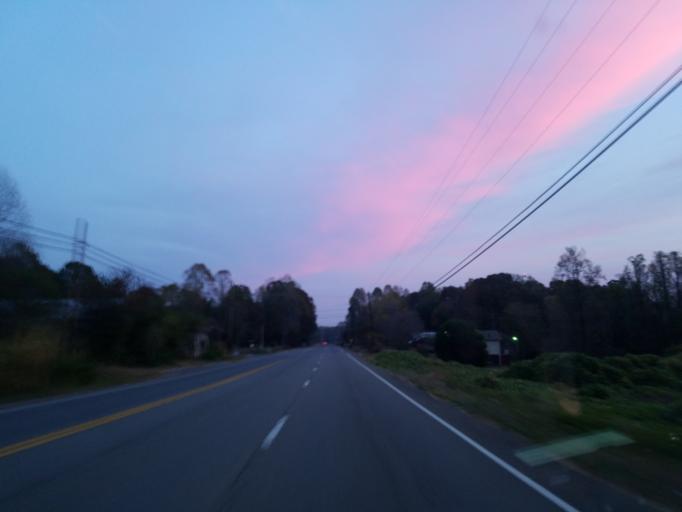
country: US
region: Georgia
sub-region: Pickens County
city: Jasper
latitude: 34.4887
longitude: -84.4596
